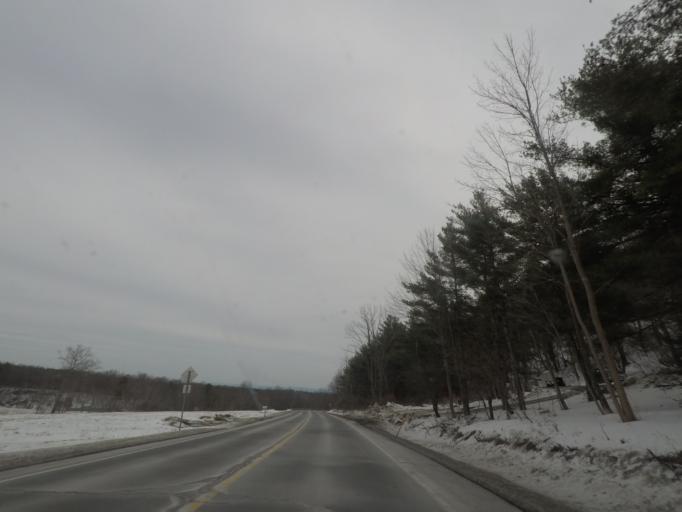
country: US
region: New York
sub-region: Albany County
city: Voorheesville
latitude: 42.5983
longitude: -73.9935
